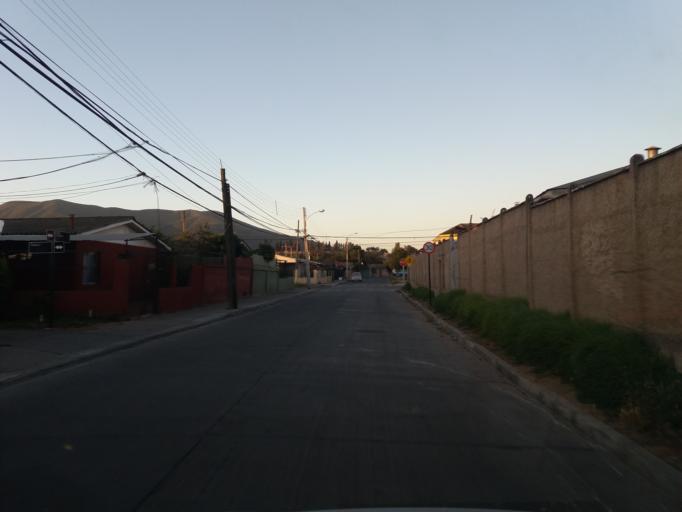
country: CL
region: Valparaiso
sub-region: Provincia de Quillota
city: Quillota
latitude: -32.8827
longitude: -71.2551
